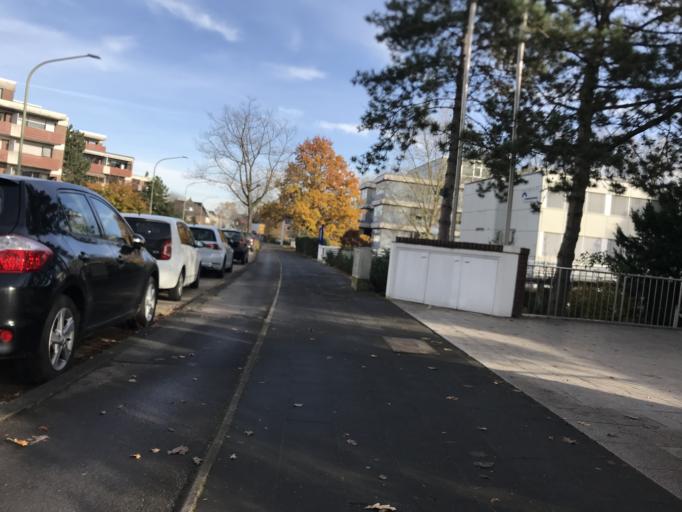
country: DE
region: North Rhine-Westphalia
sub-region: Regierungsbezirk Arnsberg
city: Hamm
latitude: 51.6843
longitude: 7.8449
